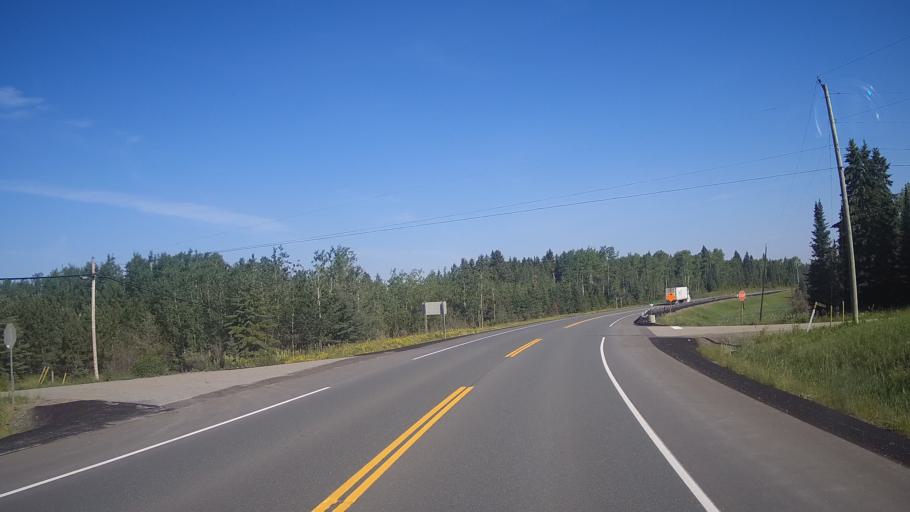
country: CA
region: Ontario
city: Dryden
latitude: 49.6693
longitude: -92.4913
